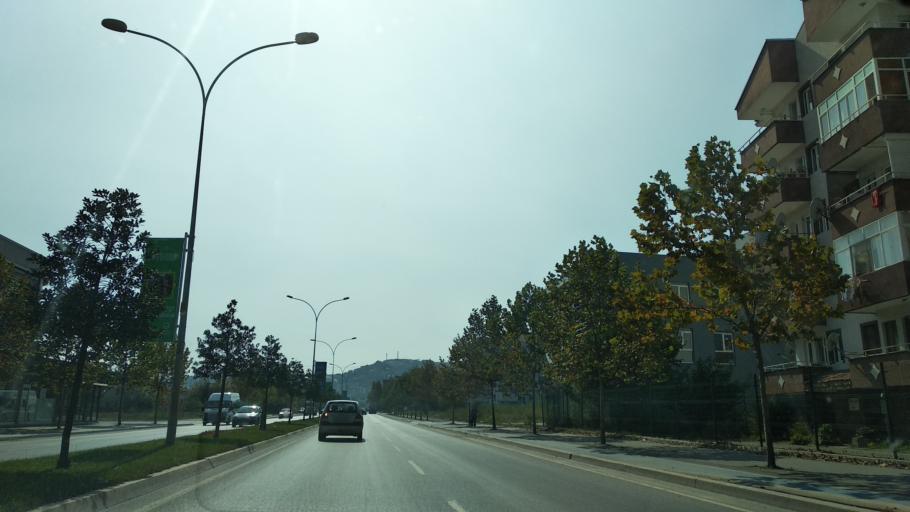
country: TR
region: Sakarya
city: Adapazari
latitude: 40.7697
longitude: 30.3640
